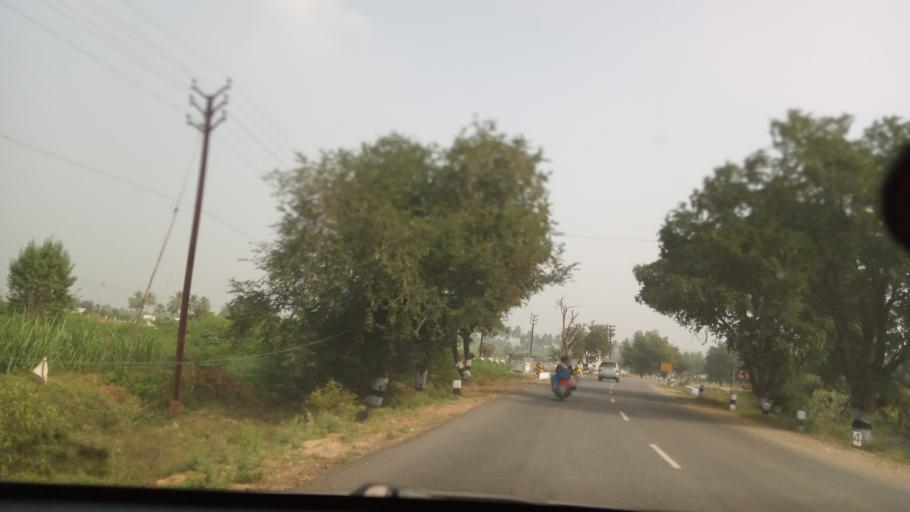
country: IN
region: Tamil Nadu
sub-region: Erode
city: Sathyamangalam
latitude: 11.4445
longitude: 77.2088
